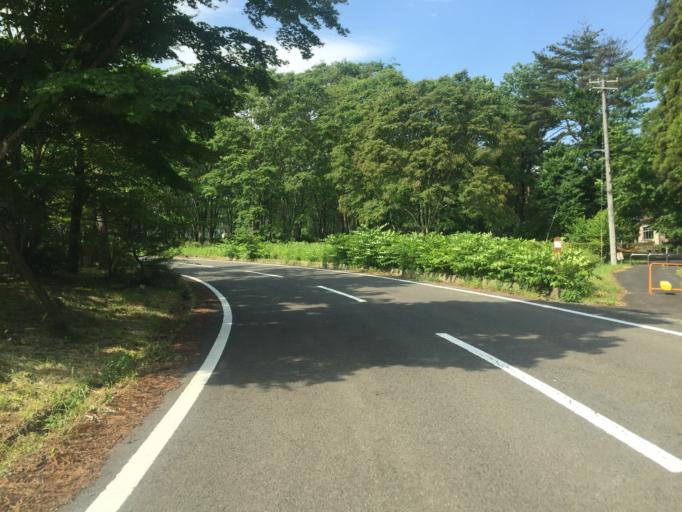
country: JP
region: Fukushima
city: Fukushima-shi
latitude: 37.7104
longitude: 140.3601
